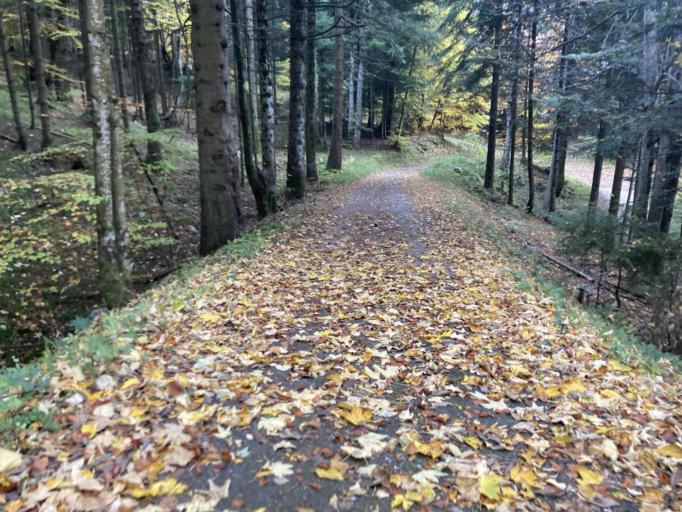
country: FR
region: Rhone-Alpes
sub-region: Departement de la Haute-Savoie
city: Veyrier-du-Lac
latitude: 45.9099
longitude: 6.1753
